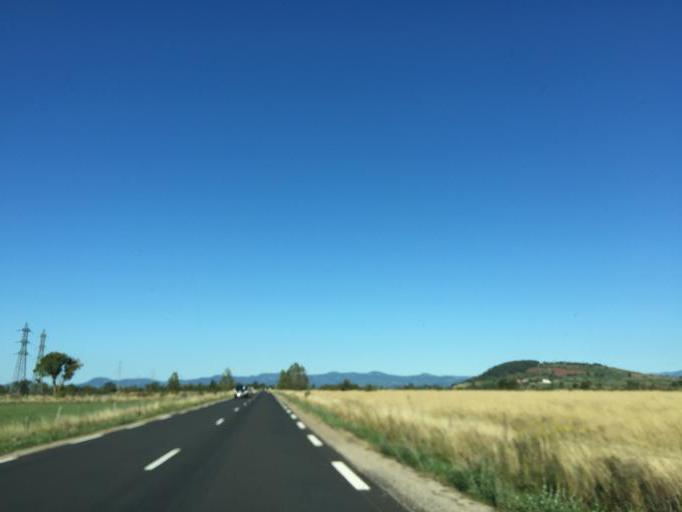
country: FR
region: Auvergne
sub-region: Departement de la Haute-Loire
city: Bains
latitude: 45.0127
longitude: 3.8186
